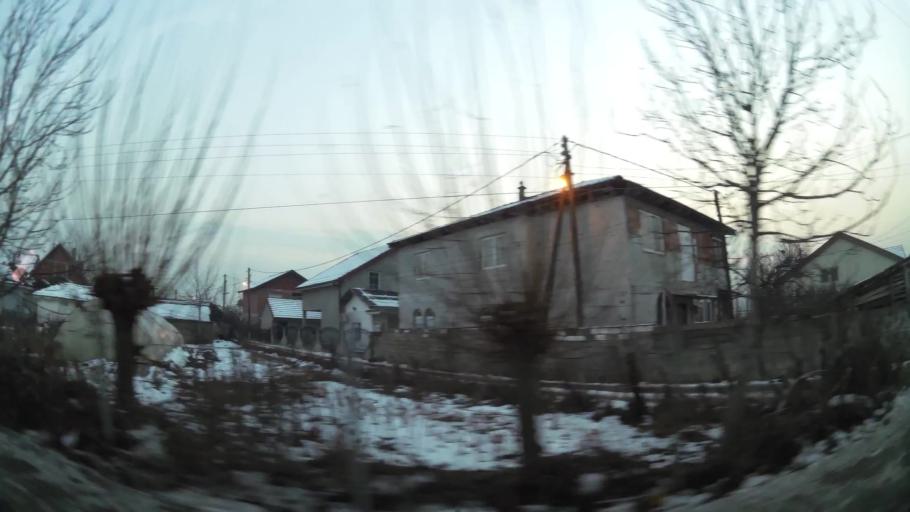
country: MK
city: Creshevo
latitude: 42.0047
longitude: 21.5119
